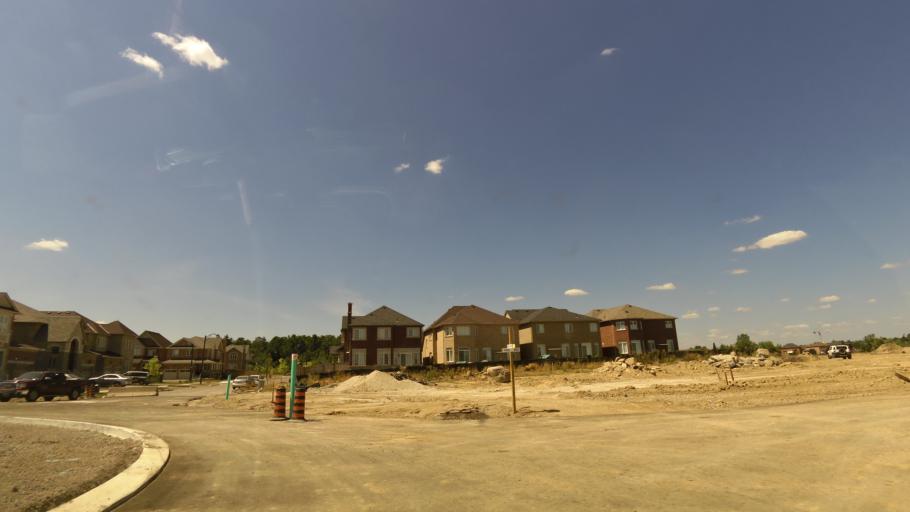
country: CA
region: Ontario
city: Brampton
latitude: 43.6349
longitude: -79.8694
